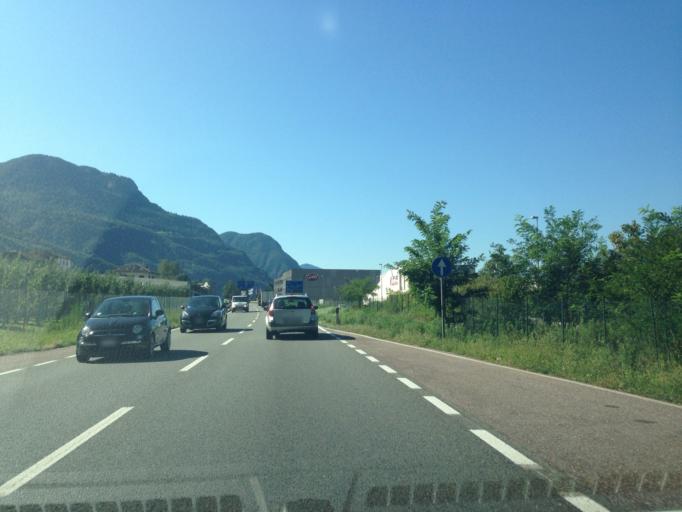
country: IT
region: Trentino-Alto Adige
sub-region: Bolzano
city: Pineta
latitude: 46.4474
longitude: 11.3436
